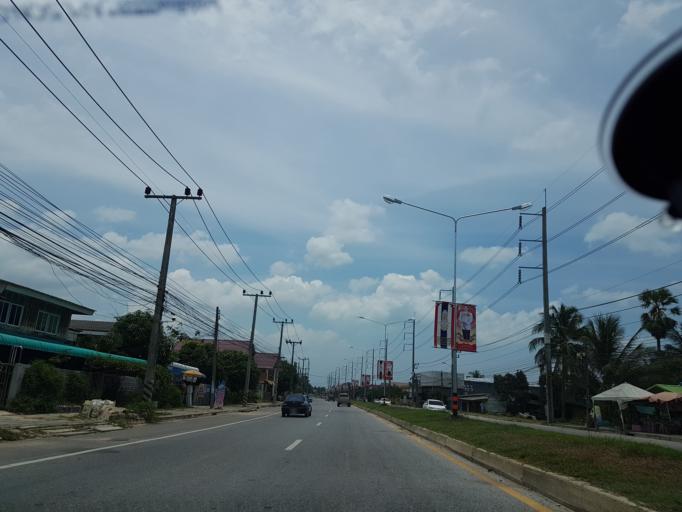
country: TH
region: Songkhla
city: Songkhla
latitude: 7.1113
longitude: 100.6328
